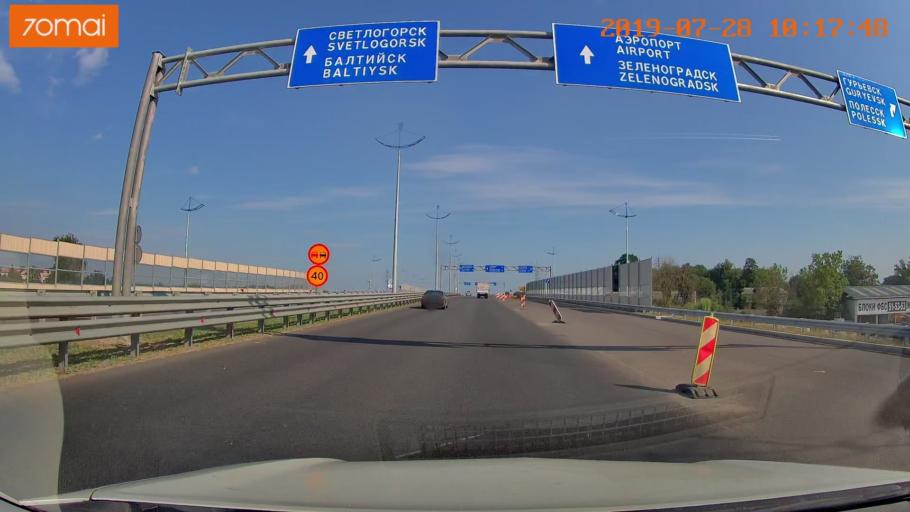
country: RU
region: Kaliningrad
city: Maloye Isakovo
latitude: 54.7445
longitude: 20.5923
